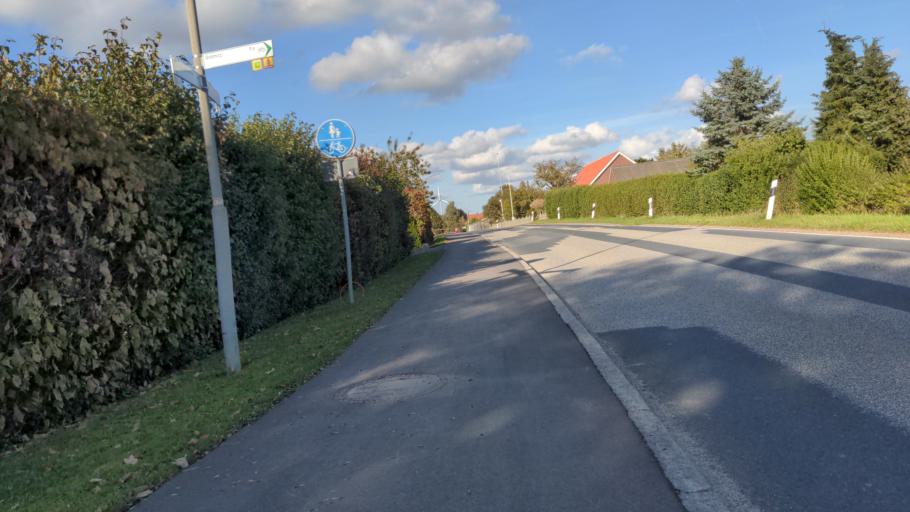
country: DE
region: Schleswig-Holstein
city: Beschendorf
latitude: 54.1794
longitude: 10.8775
